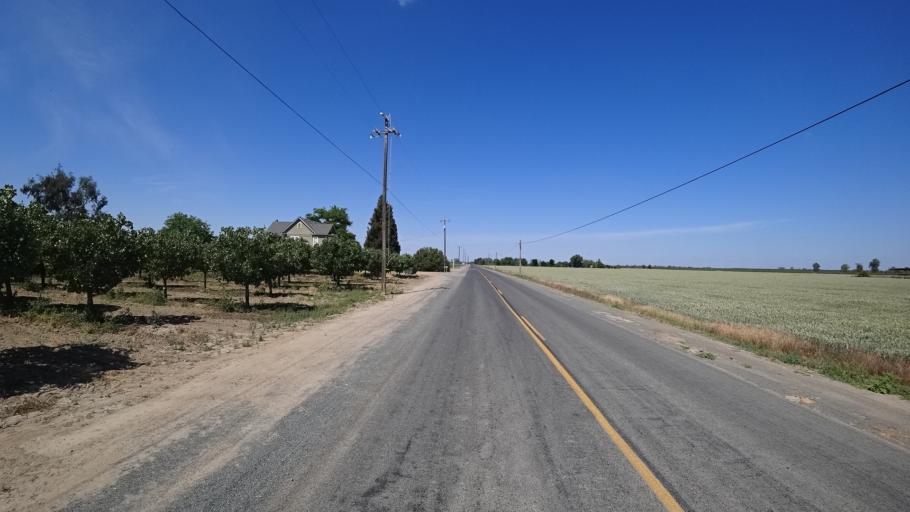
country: US
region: California
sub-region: Kings County
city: Armona
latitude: 36.2693
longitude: -119.7094
